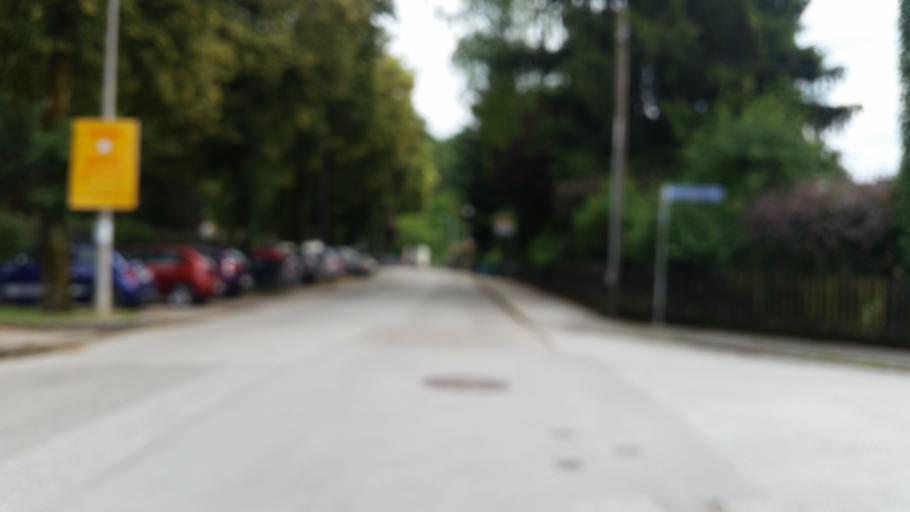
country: AT
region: Salzburg
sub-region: Salzburg Stadt
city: Salzburg
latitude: 47.8124
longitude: 13.0721
